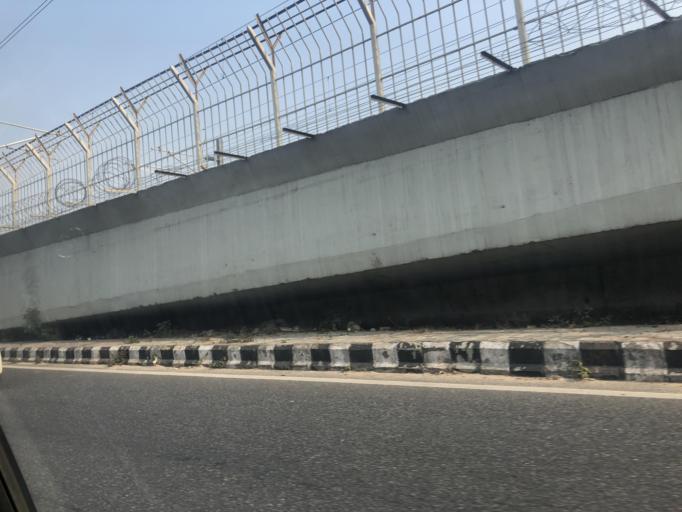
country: IN
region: NCT
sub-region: Central Delhi
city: Karol Bagh
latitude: 28.6121
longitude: 77.1376
